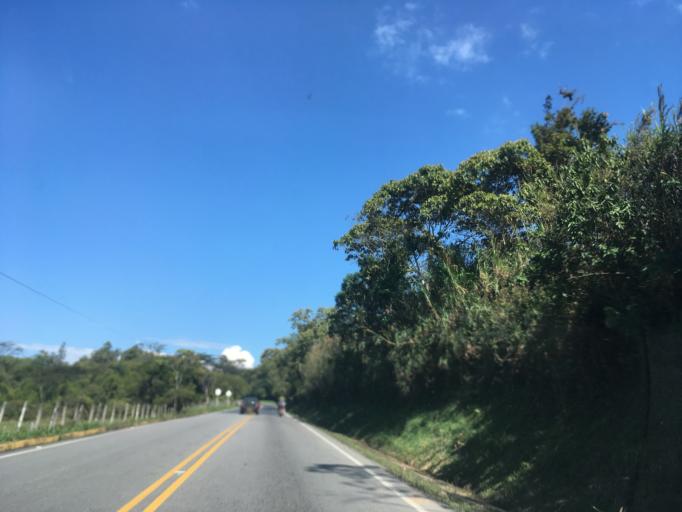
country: CO
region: Santander
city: Suaita
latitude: 6.0819
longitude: -73.3902
